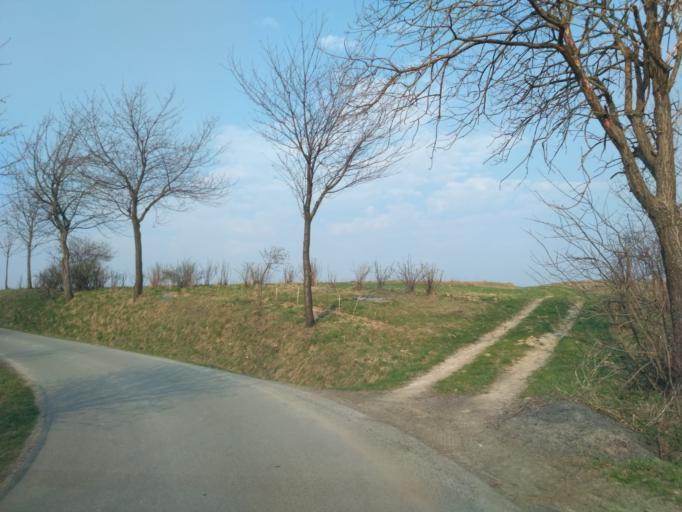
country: PL
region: Subcarpathian Voivodeship
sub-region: Powiat ropczycko-sedziszowski
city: Wielopole Skrzynskie
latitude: 49.9114
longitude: 21.5995
